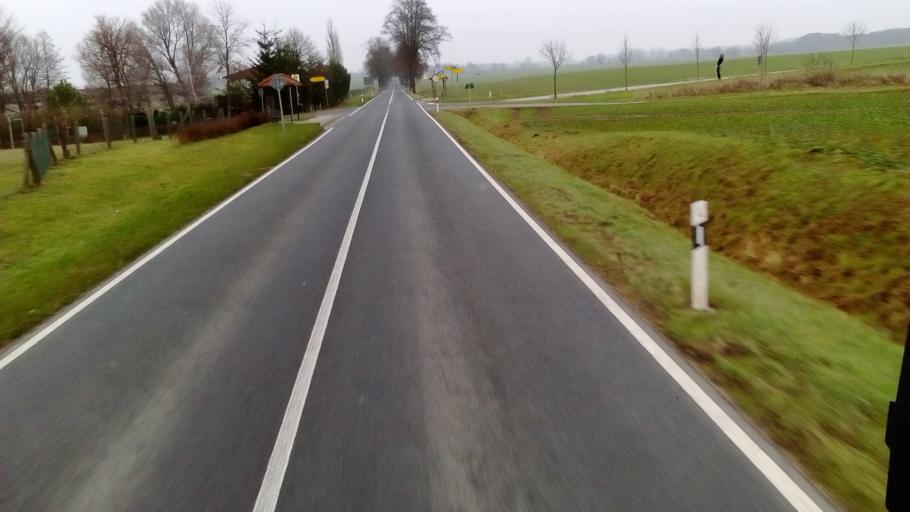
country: DE
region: Mecklenburg-Vorpommern
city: Loitz
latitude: 53.4366
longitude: 13.4635
